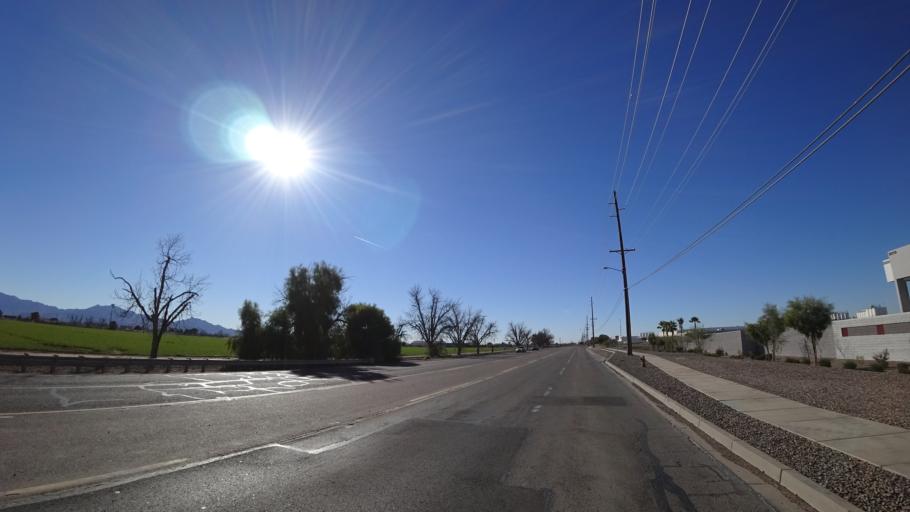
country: US
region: Arizona
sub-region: Maricopa County
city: Tolleson
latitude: 33.4358
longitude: -112.2601
